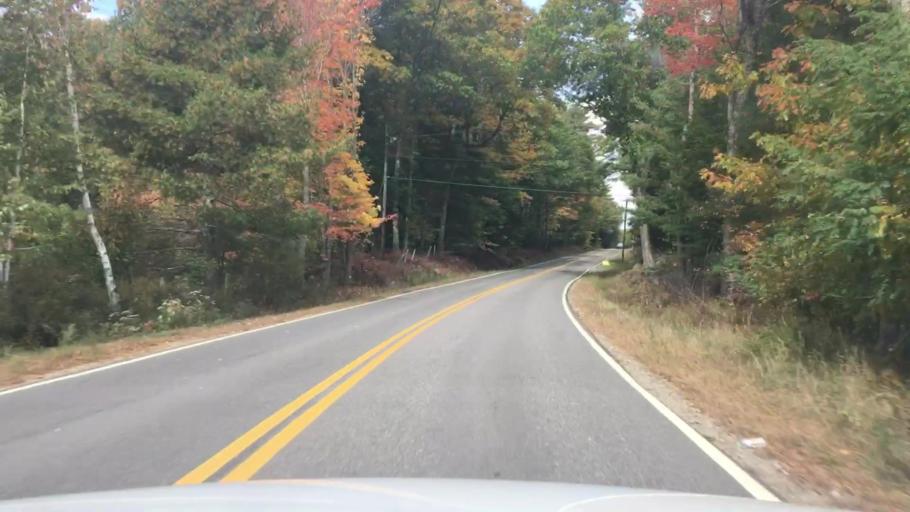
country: US
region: Maine
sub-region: Knox County
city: Hope
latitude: 44.2451
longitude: -69.1230
